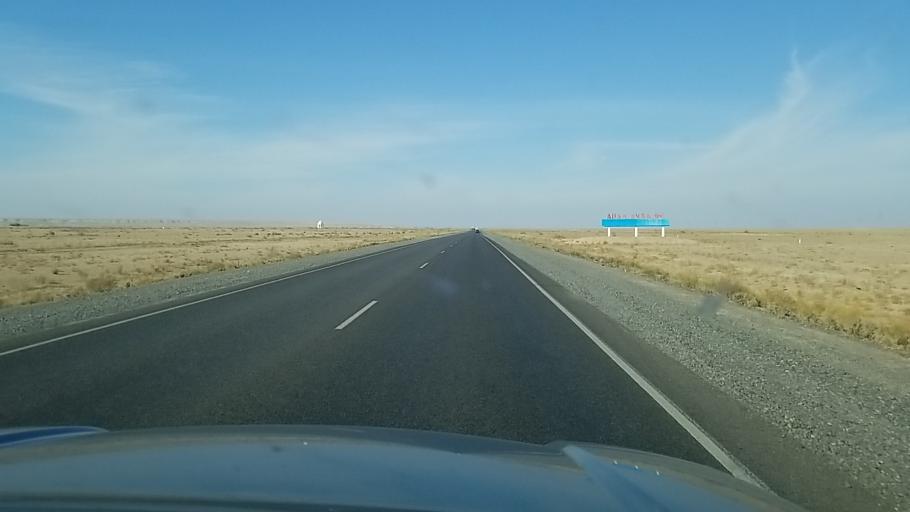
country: KZ
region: Qyzylorda
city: Ayteke Bi
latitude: 46.0680
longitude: 62.0994
